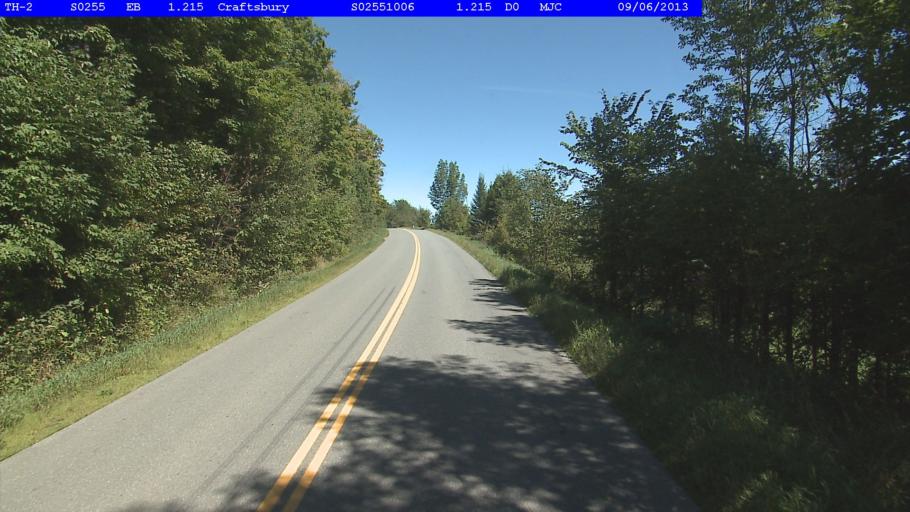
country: US
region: Vermont
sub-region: Caledonia County
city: Hardwick
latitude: 44.6350
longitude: -72.3473
